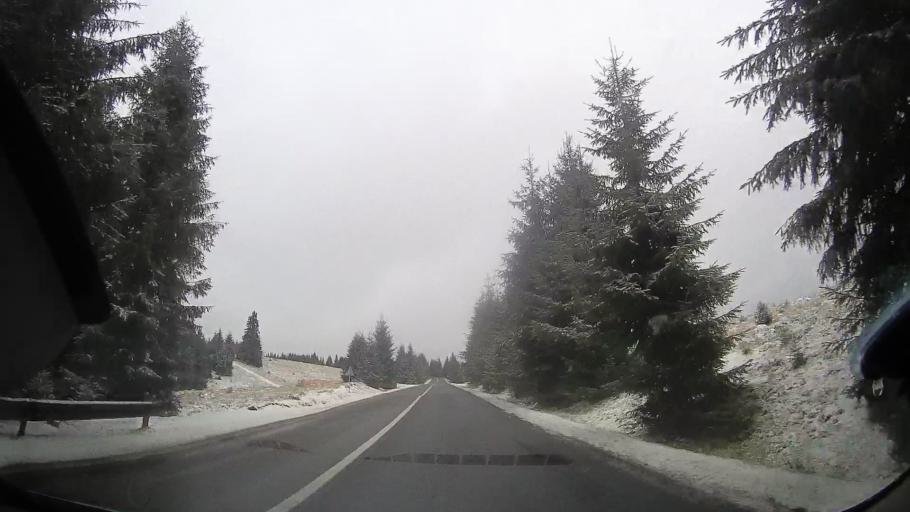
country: RO
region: Cluj
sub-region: Comuna Belis
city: Belis
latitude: 46.6749
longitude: 23.0452
